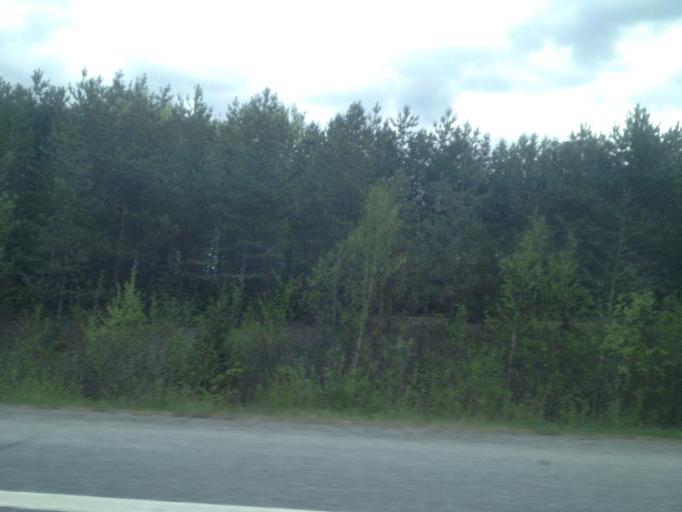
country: FI
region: Haeme
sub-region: Haemeenlinna
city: Haemeenlinna
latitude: 60.9636
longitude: 24.4800
